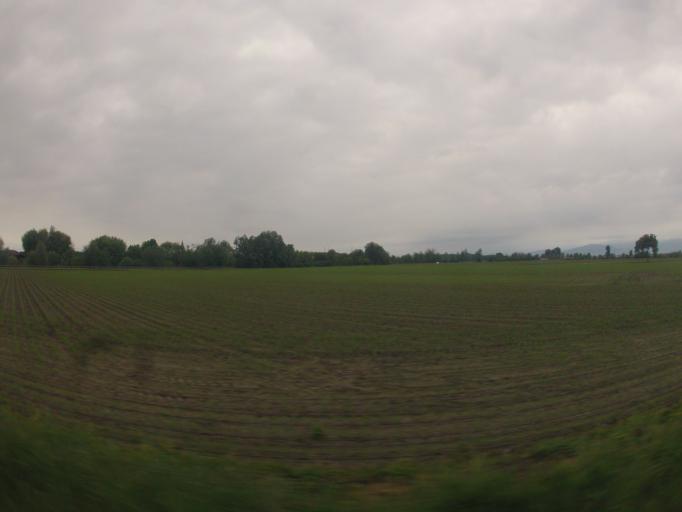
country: IT
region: Piedmont
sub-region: Provincia di Cuneo
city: Polonghera
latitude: 44.8022
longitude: 7.5953
